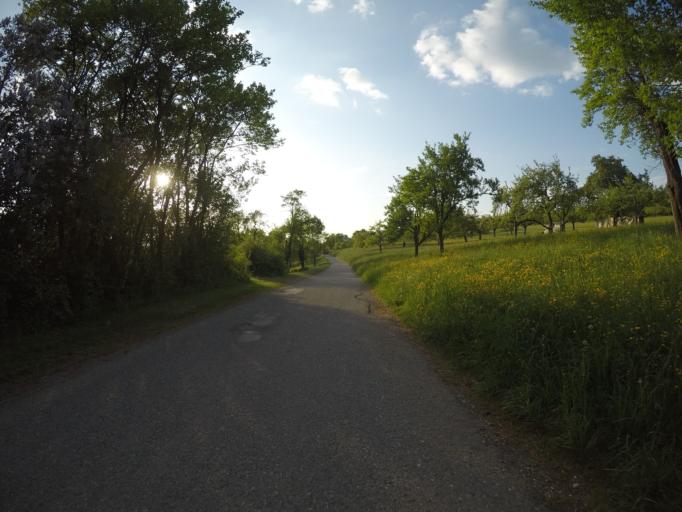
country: DE
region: Baden-Wuerttemberg
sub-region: Tuebingen Region
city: Pfullingen
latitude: 48.4533
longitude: 9.2391
